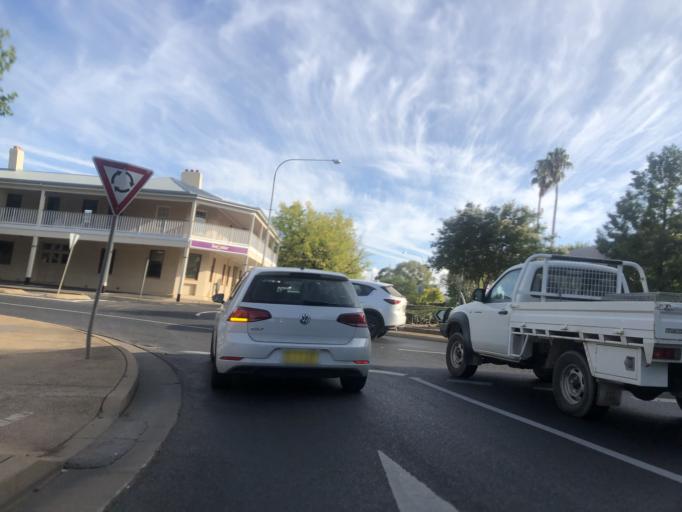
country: AU
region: New South Wales
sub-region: Orange Municipality
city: Orange
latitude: -33.2820
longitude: 149.1015
